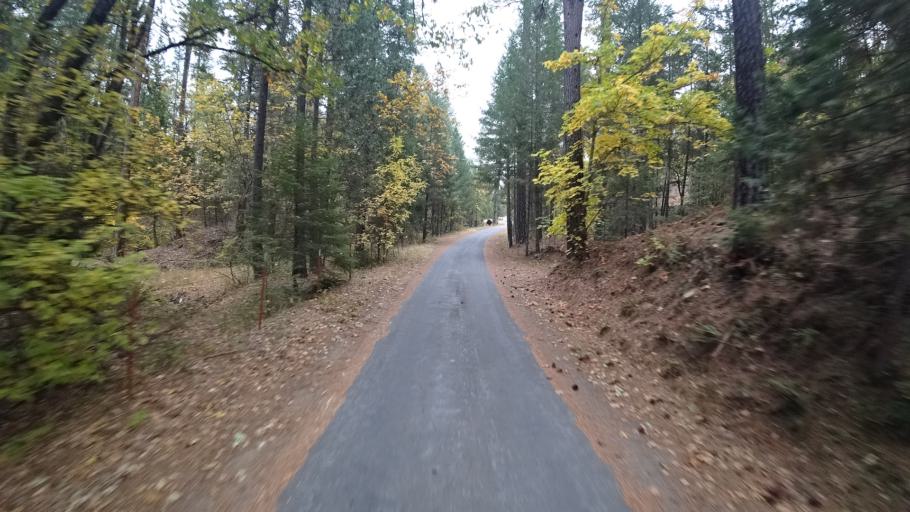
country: US
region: California
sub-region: Siskiyou County
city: Happy Camp
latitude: 41.8382
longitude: -123.2041
